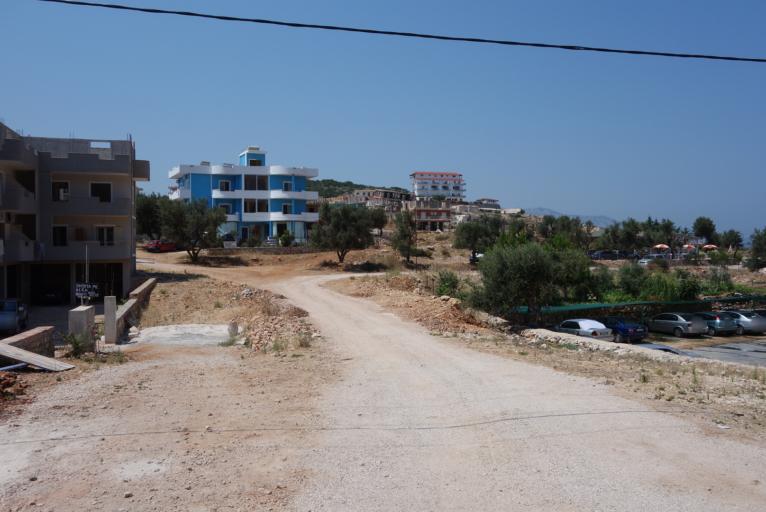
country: AL
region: Vlore
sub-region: Rrethi i Sarandes
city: Xarre
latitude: 39.7789
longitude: 20.0082
